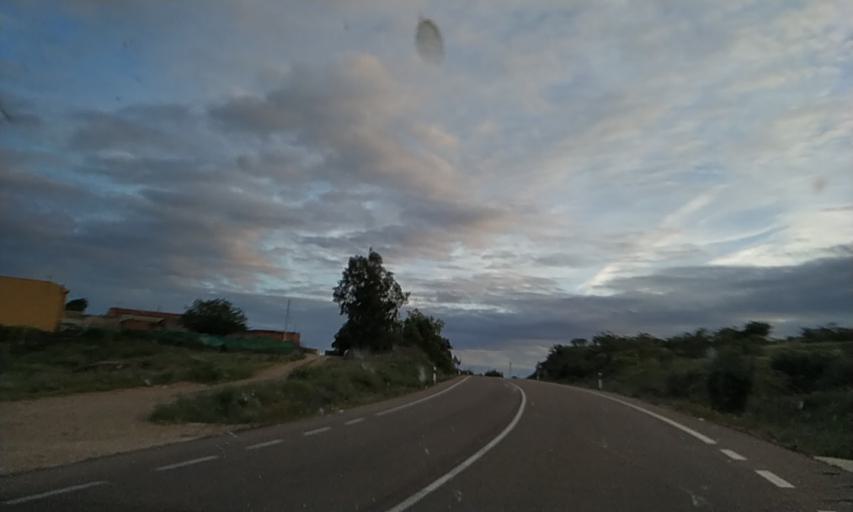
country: ES
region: Extremadura
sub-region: Provincia de Badajoz
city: La Roca de la Sierra
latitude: 39.1120
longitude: -6.6921
